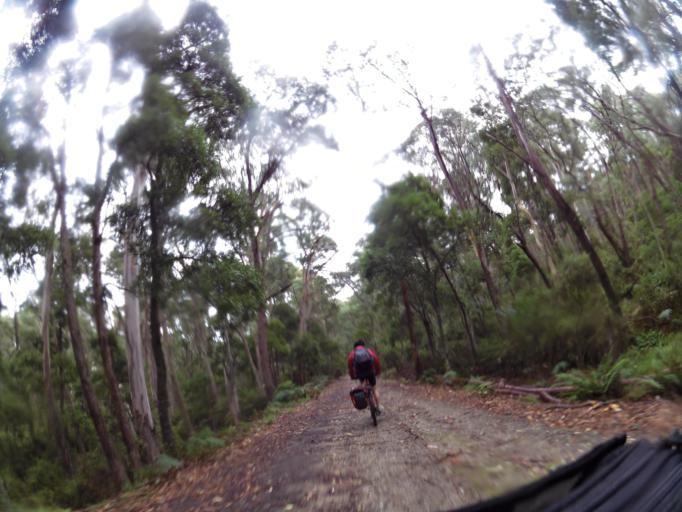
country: AU
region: New South Wales
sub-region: Greater Hume Shire
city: Holbrook
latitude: -36.1954
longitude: 147.5212
